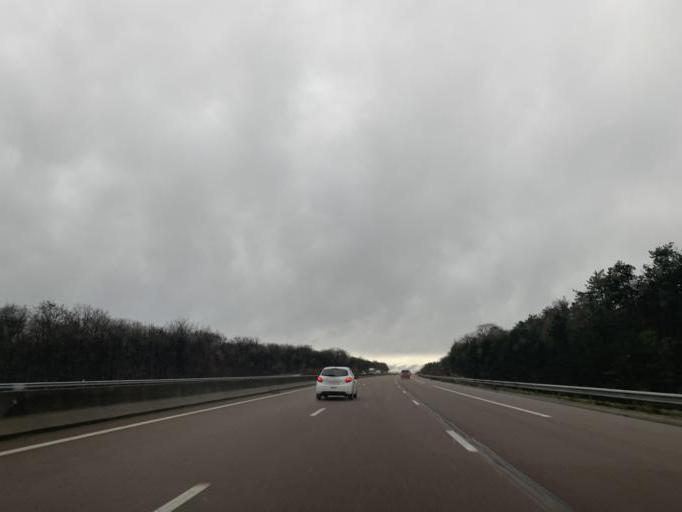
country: FR
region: Bourgogne
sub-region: Departement de la Cote-d'Or
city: Selongey
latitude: 47.6251
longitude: 5.1787
